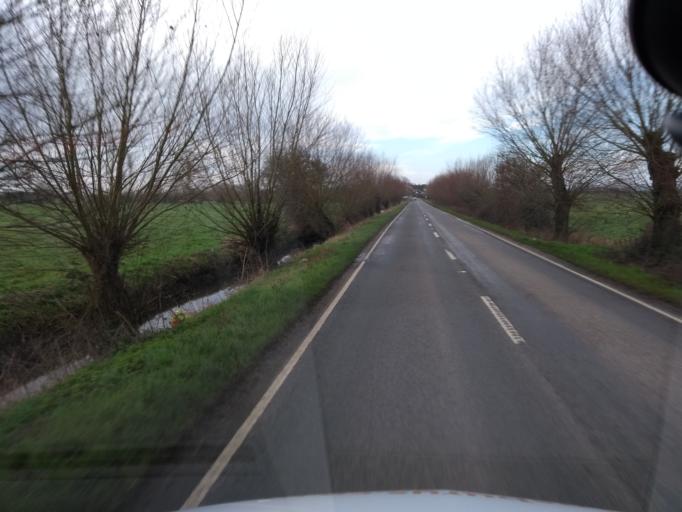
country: GB
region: England
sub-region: Somerset
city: Westonzoyland
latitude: 51.1006
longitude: -2.8708
